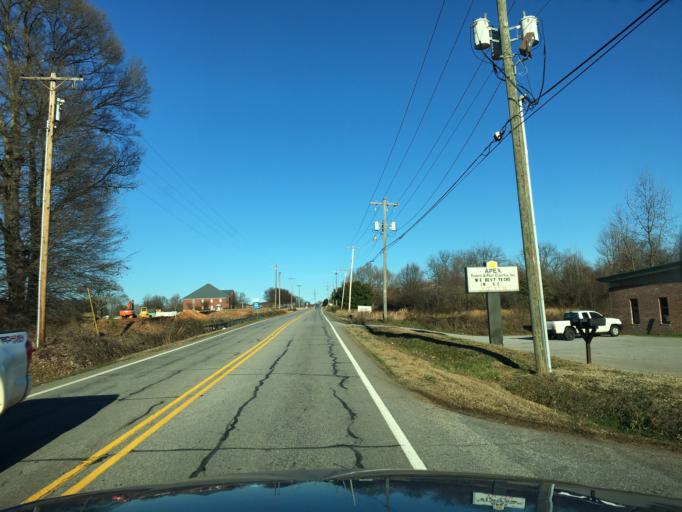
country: US
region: South Carolina
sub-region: Greenville County
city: Greer
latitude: 34.9220
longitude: -82.2537
